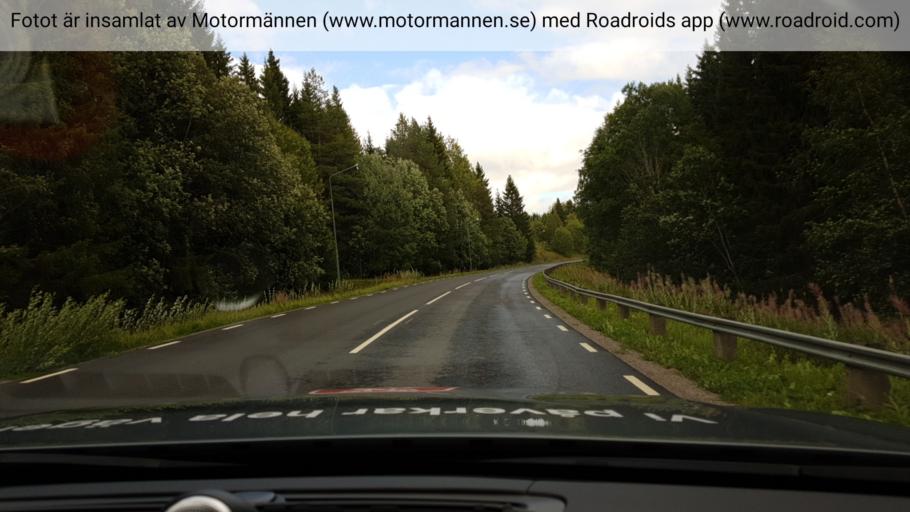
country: SE
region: Jaemtland
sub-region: Krokoms Kommun
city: Krokom
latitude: 63.6767
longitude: 14.5843
